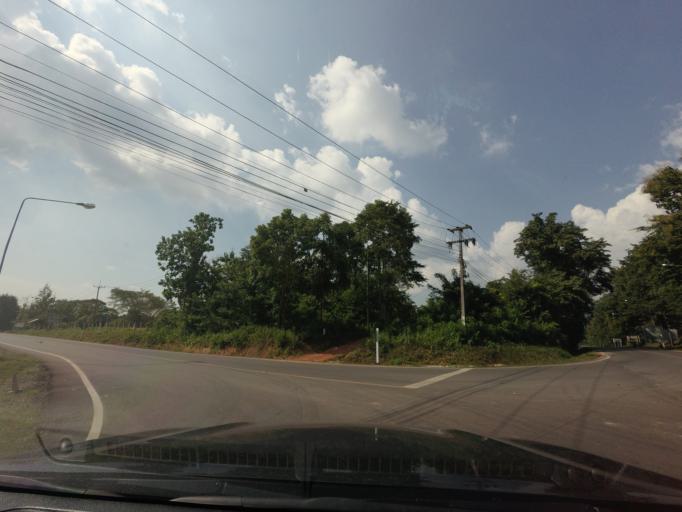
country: TH
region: Nan
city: Santi Suk
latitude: 18.9862
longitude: 100.9396
